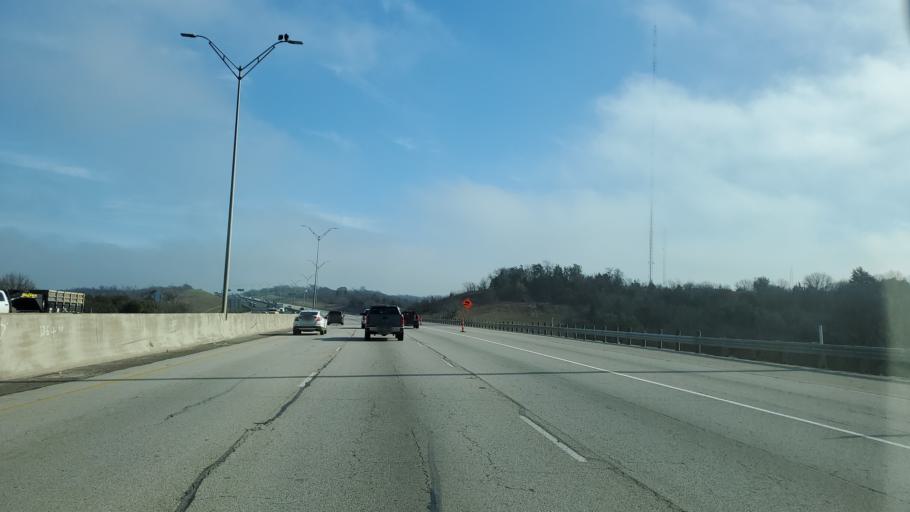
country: US
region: Texas
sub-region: Tarrant County
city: Haltom City
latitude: 32.7511
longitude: -97.2768
